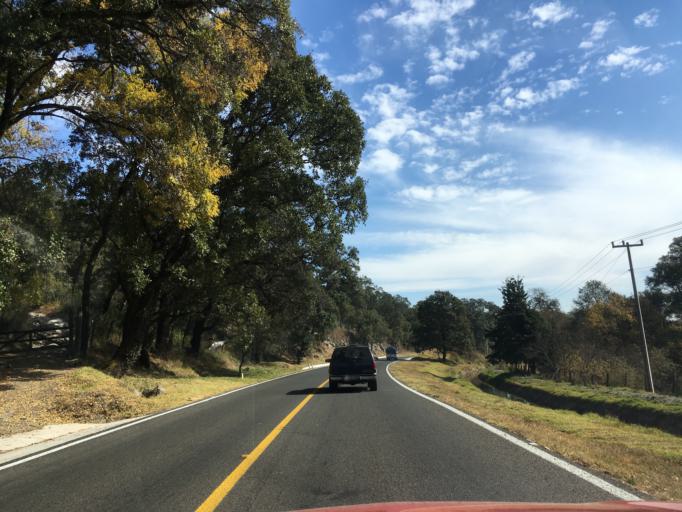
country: MX
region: Michoacan
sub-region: Hidalgo
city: San Lucas Huarirapeo (La Mesa de San Lucas)
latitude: 19.6771
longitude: -100.6586
